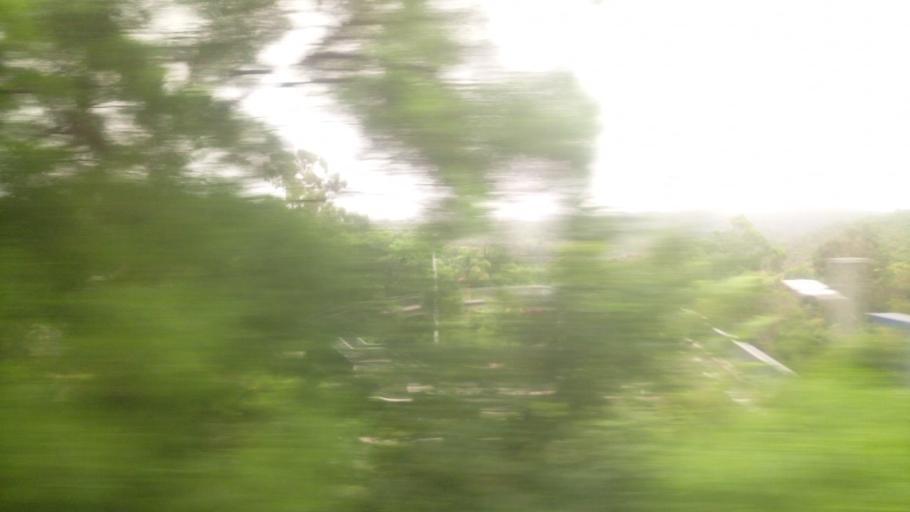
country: AU
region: New South Wales
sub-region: Blue Mountains Municipality
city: Hazelbrook
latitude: -33.7357
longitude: 150.4816
